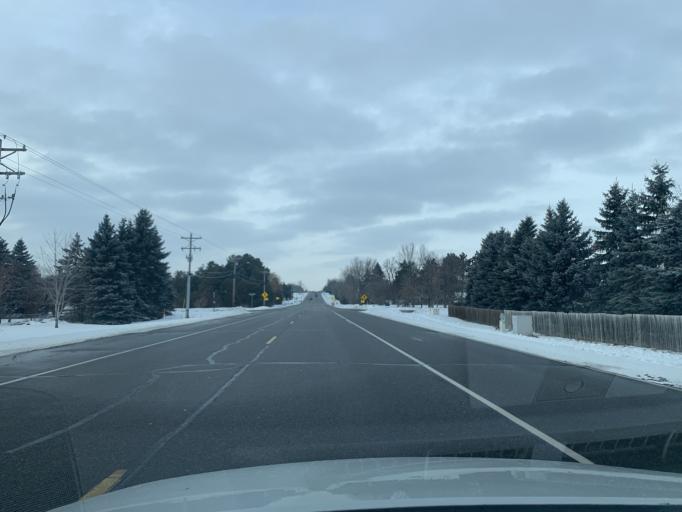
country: US
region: Minnesota
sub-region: Anoka County
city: Anoka
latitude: 45.2379
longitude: -93.4080
